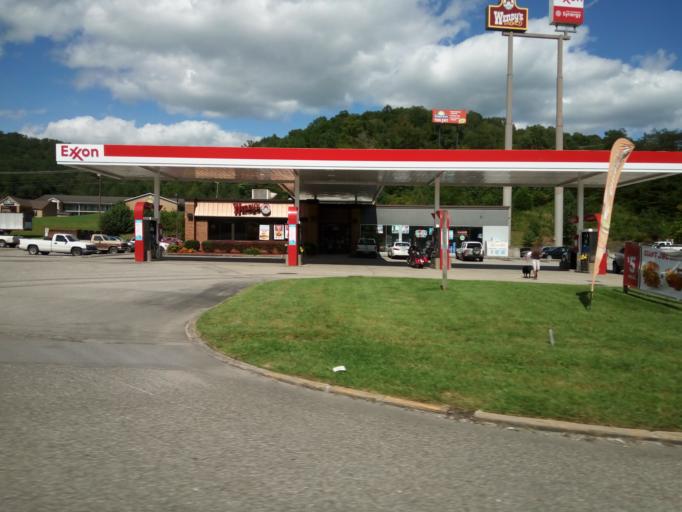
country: US
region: Tennessee
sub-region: Campbell County
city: Jellico
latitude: 36.5809
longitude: -84.1137
